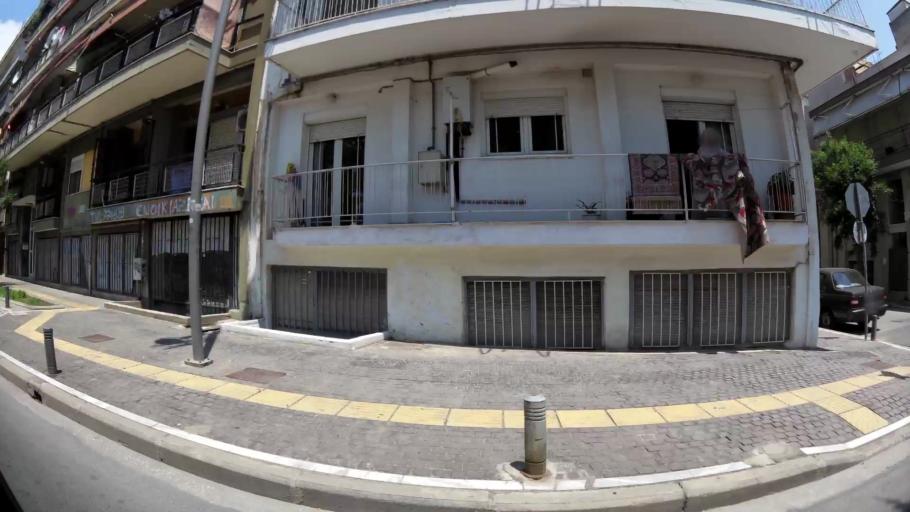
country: GR
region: Central Macedonia
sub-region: Nomos Thessalonikis
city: Ampelokipoi
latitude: 40.6510
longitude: 22.9194
